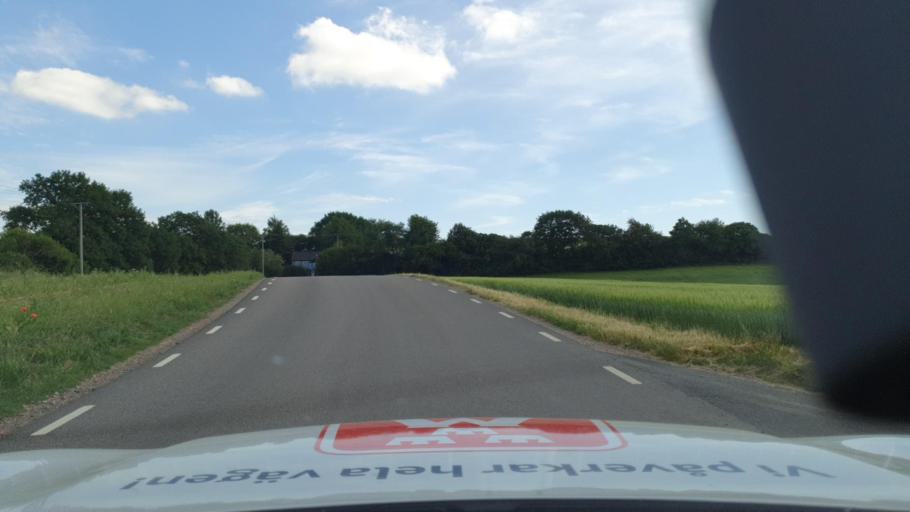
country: SE
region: Skane
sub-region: Skurups Kommun
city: Skurup
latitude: 55.5296
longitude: 13.5459
